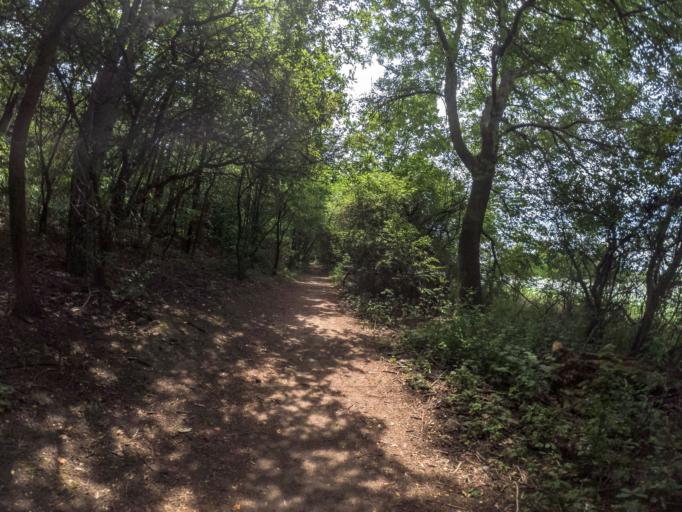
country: CZ
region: Central Bohemia
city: Neratovice
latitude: 50.2436
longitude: 14.5167
